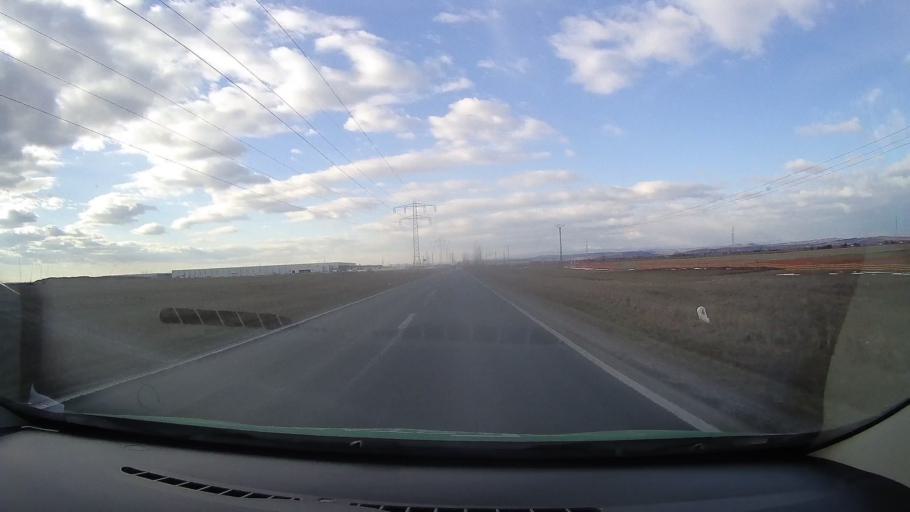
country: RO
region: Dambovita
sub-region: Comuna Comisani
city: Lazuri
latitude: 44.8705
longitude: 25.5239
